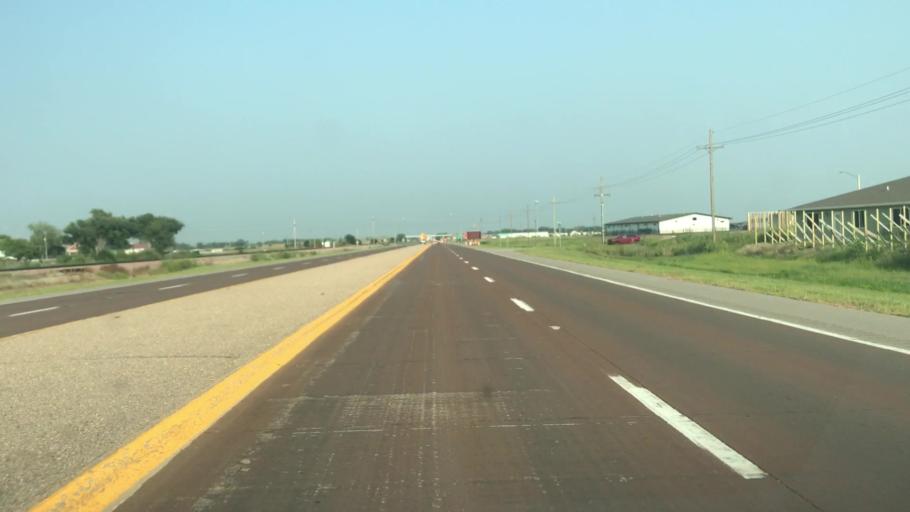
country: US
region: Nebraska
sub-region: Hall County
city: Grand Island
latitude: 40.9575
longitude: -98.4024
